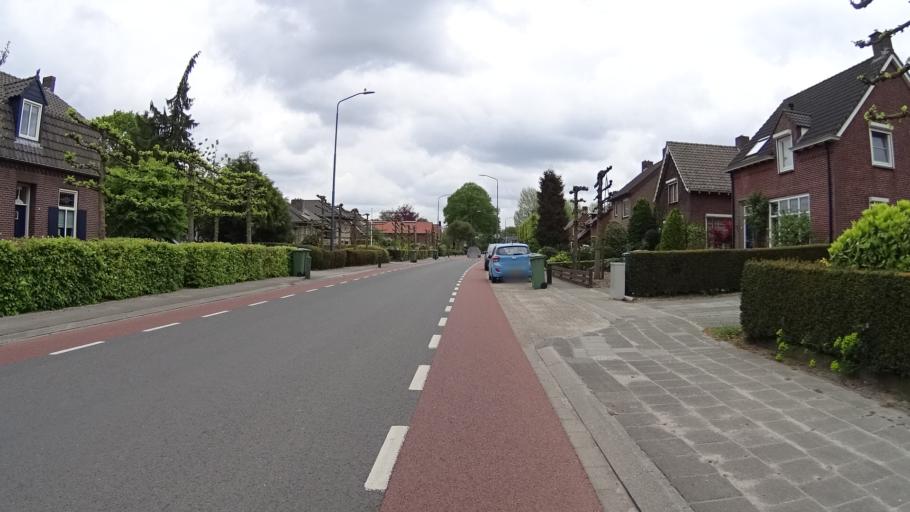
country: NL
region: North Brabant
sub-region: Gemeente Boekel
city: Boekel
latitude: 51.6020
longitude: 5.6639
